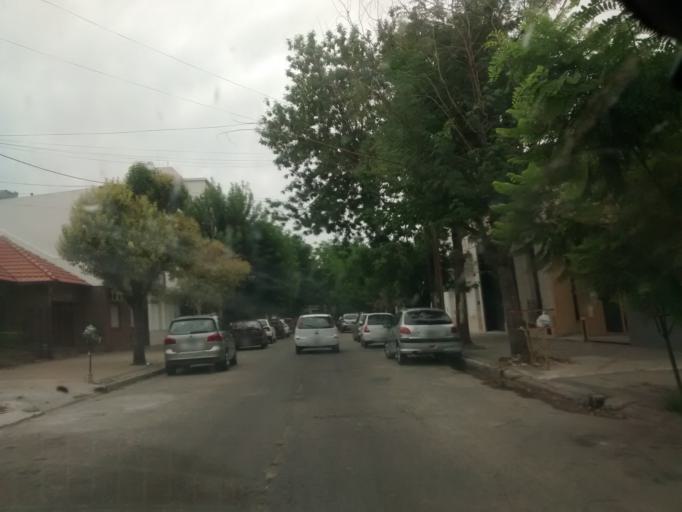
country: AR
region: Buenos Aires
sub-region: Partido de La Plata
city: La Plata
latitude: -34.9293
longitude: -57.9363
